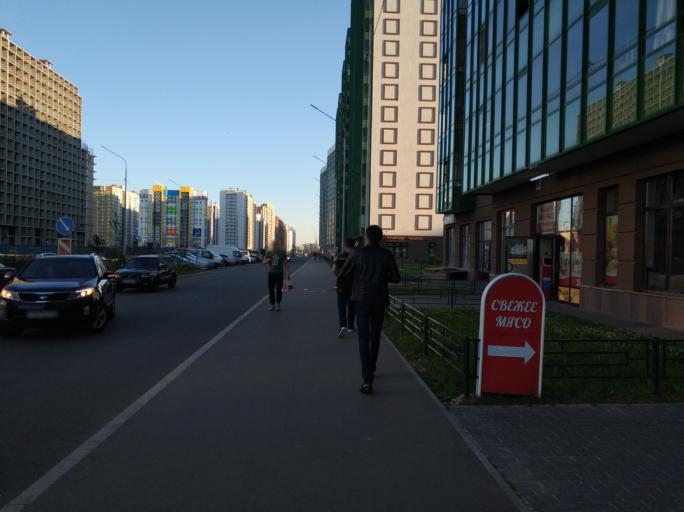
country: RU
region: Leningrad
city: Murino
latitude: 60.0645
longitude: 30.4339
